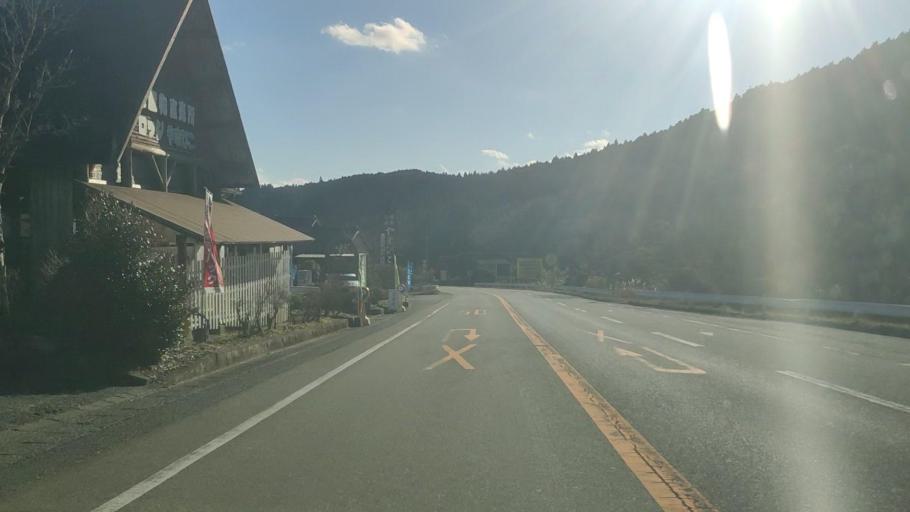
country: JP
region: Fukuoka
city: Maebaru-chuo
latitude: 33.4604
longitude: 130.2742
